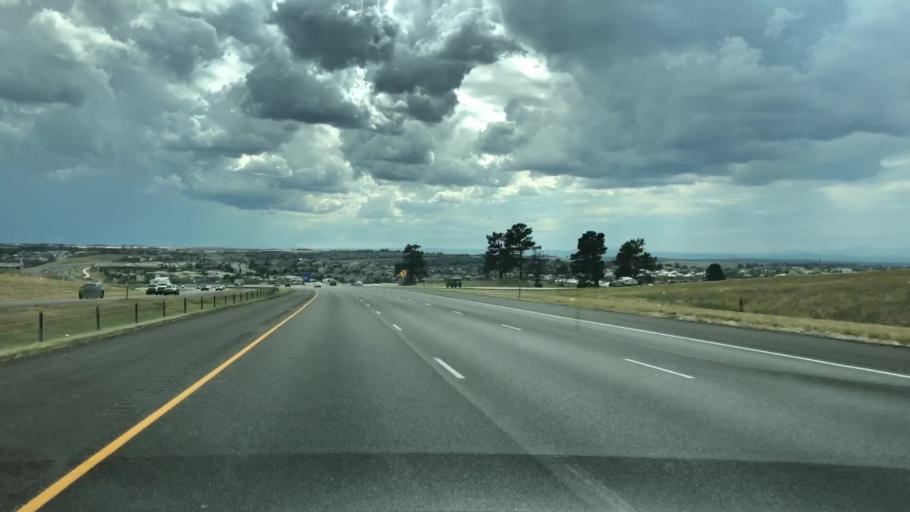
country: US
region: Colorado
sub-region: Douglas County
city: Parker
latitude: 39.5926
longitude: -104.7083
